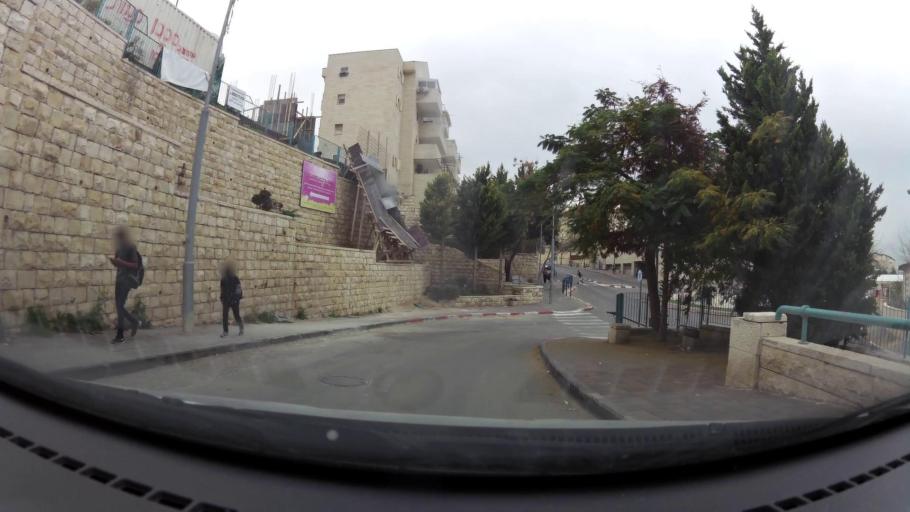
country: IL
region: Jerusalem
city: Bet Shemesh
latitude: 31.7140
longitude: 34.9954
